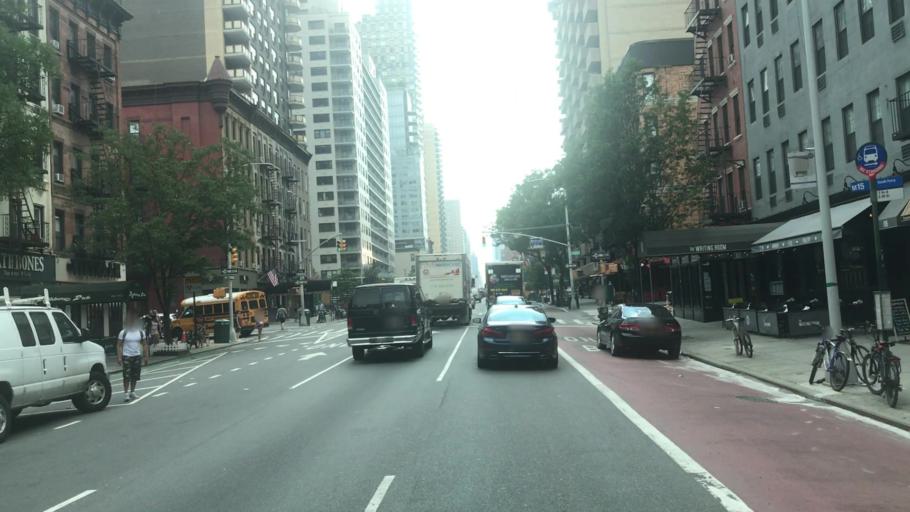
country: US
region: New York
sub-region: New York County
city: Manhattan
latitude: 40.7798
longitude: -73.9505
